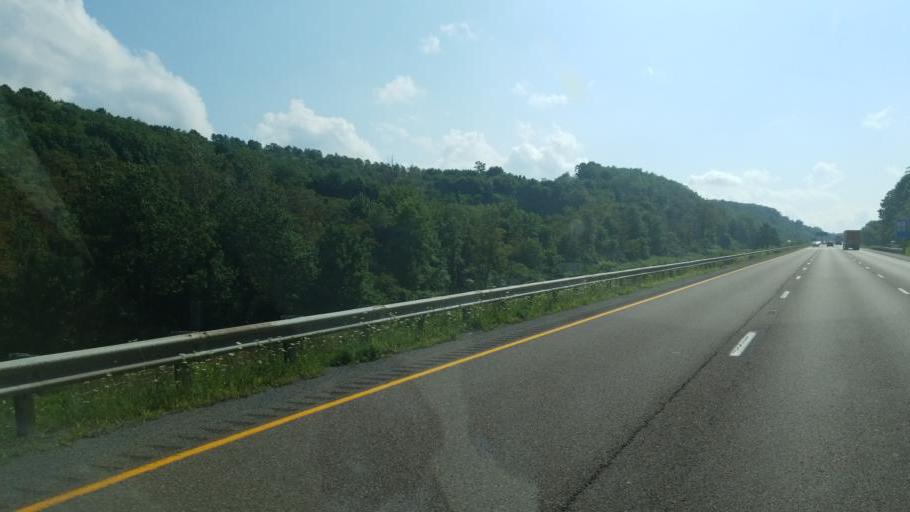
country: US
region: Maryland
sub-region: Allegany County
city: Frostburg
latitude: 39.6377
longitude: -78.8990
